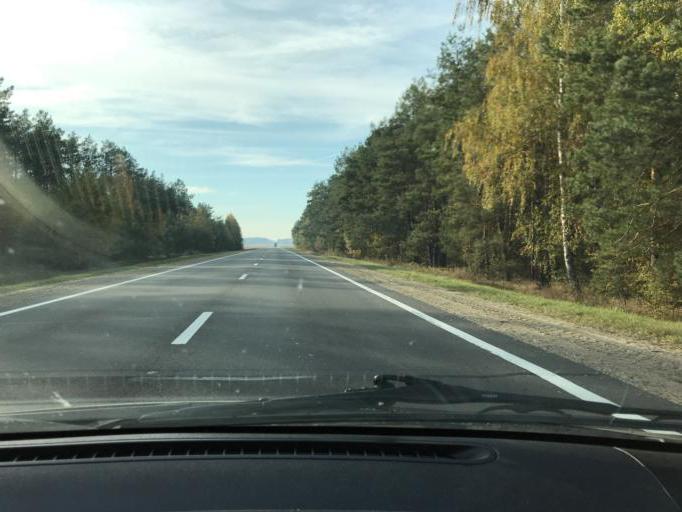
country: BY
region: Brest
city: Horad Pinsk
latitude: 52.1486
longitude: 25.8862
